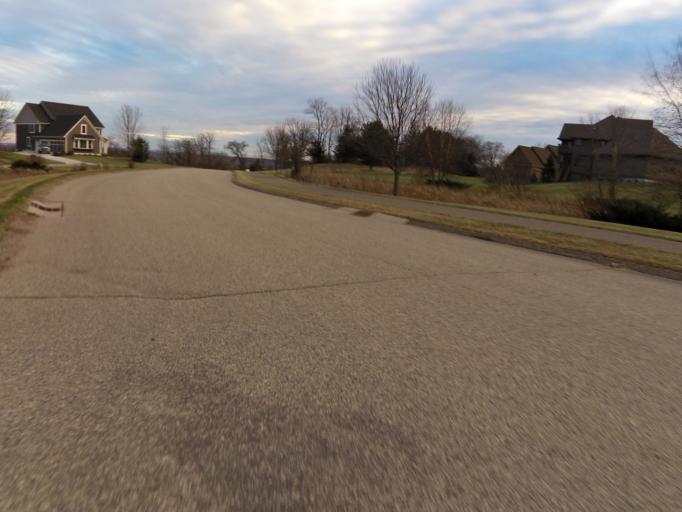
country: US
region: Minnesota
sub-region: Washington County
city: Bayport
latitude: 44.9992
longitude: -92.7948
